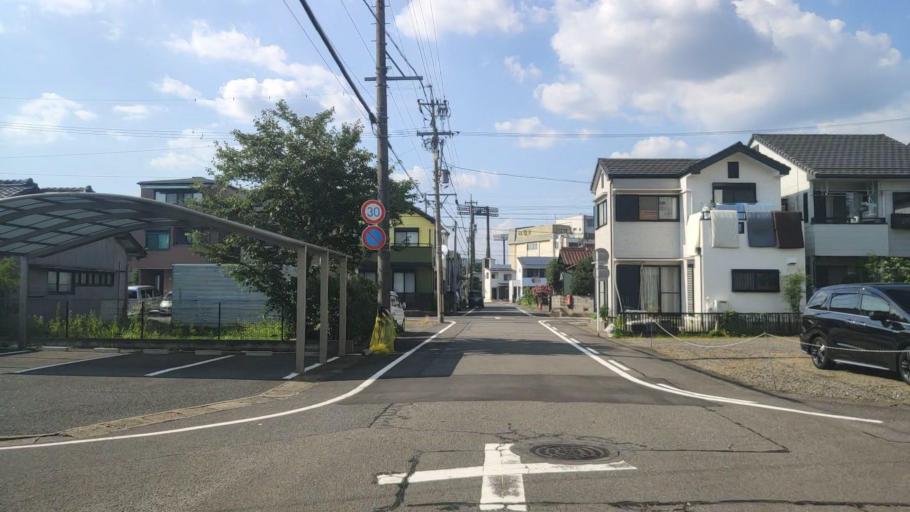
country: JP
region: Gifu
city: Gifu-shi
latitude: 35.4369
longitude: 136.7640
